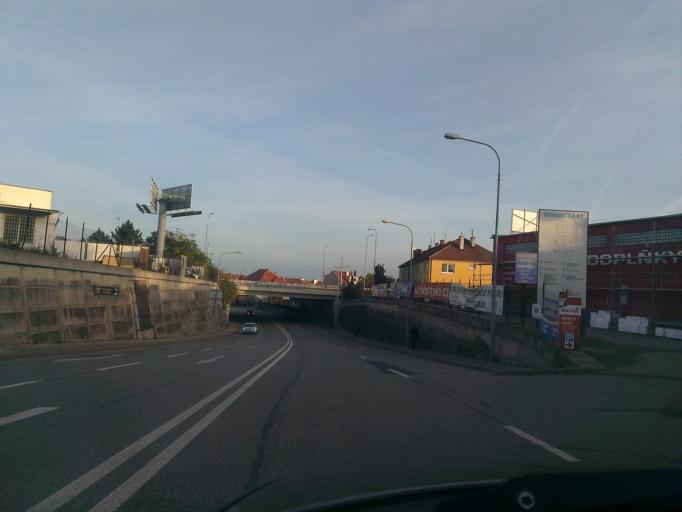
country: CZ
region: South Moravian
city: Moravany
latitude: 49.1633
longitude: 16.5975
